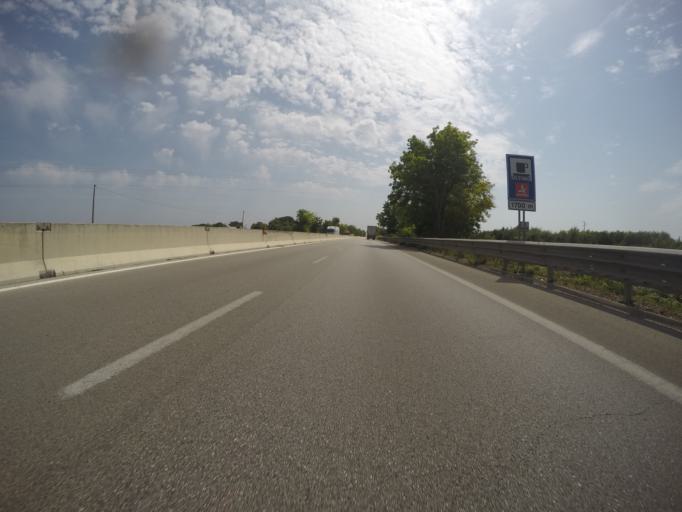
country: IT
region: Apulia
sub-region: Provincia di Brindisi
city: Oria
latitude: 40.5335
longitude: 17.6287
